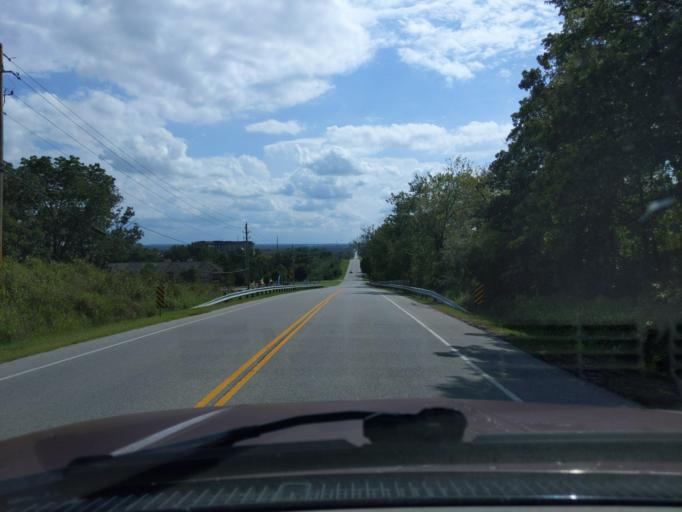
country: US
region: Oklahoma
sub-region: Tulsa County
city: Jenks
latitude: 36.0531
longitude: -96.0117
